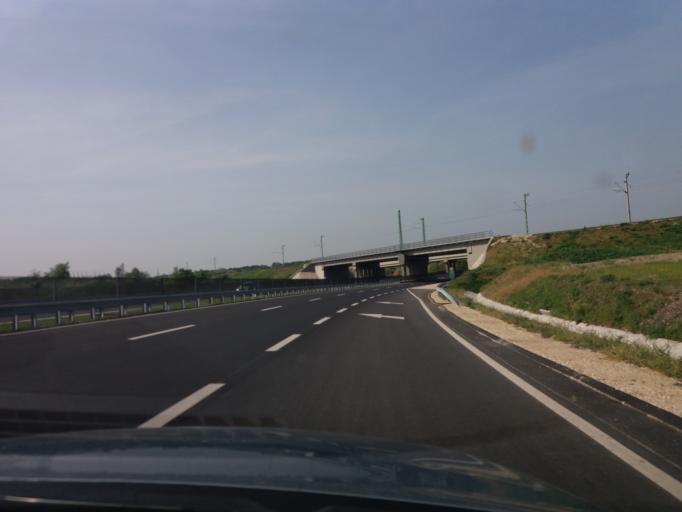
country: HU
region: Veszprem
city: Varpalota
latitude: 47.1844
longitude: 18.1351
